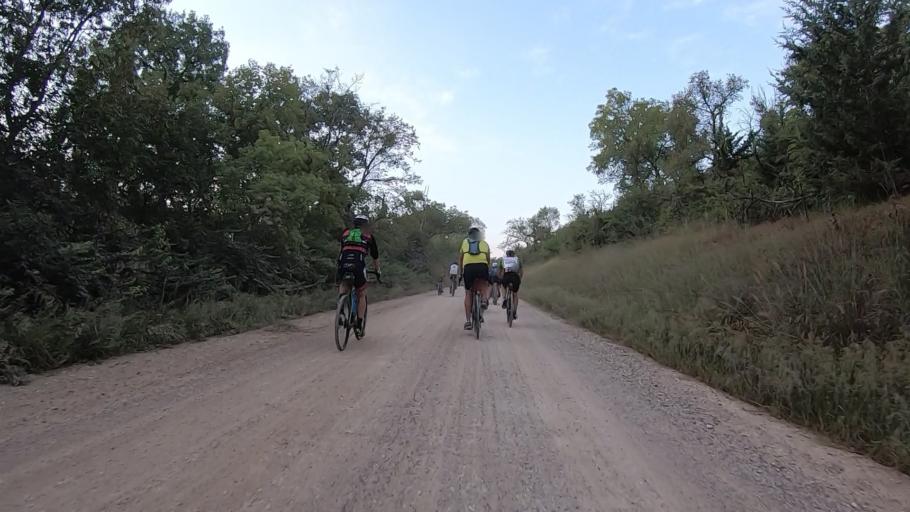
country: US
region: Kansas
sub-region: Marshall County
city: Marysville
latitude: 39.8346
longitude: -96.6654
